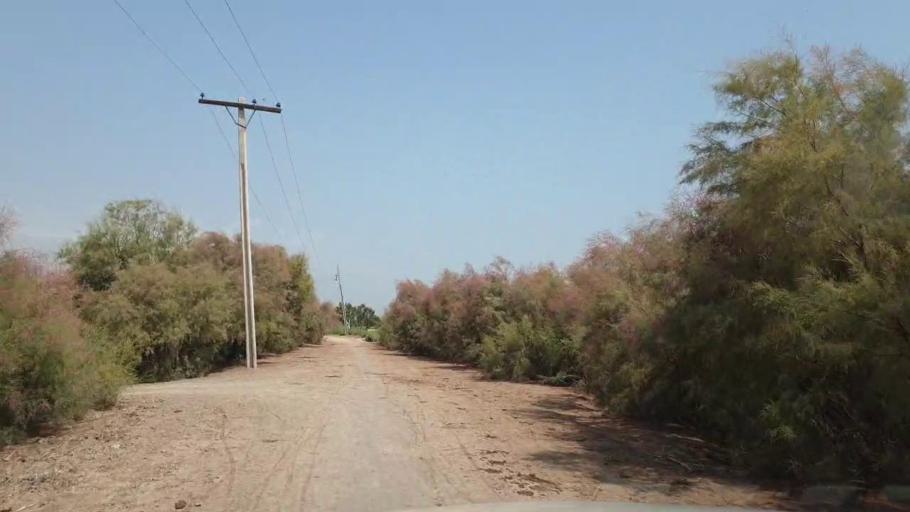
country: PK
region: Sindh
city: Ratodero
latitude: 27.8417
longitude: 68.2471
